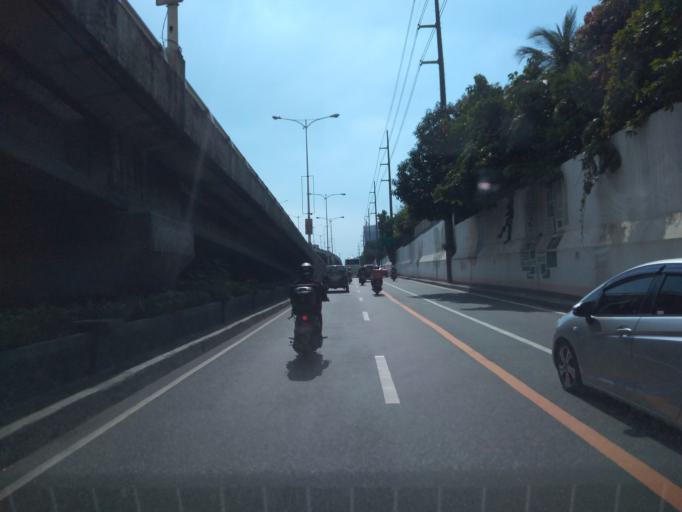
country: PH
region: Metro Manila
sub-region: Makati City
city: Makati City
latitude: 14.5574
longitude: 121.0375
